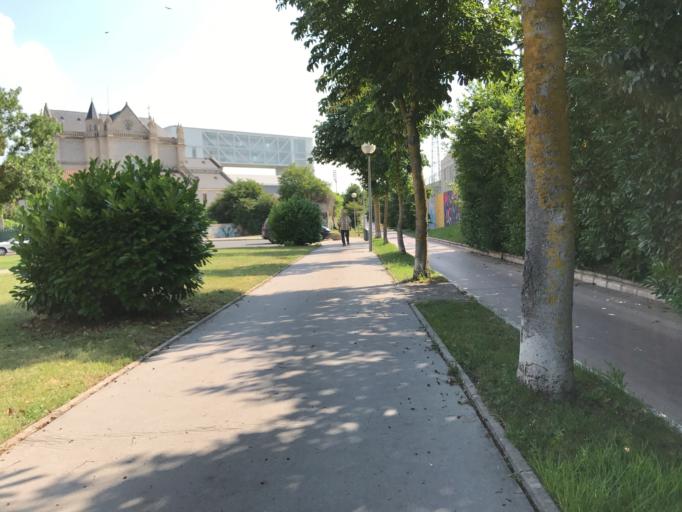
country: ES
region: Basque Country
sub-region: Provincia de Alava
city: Gasteiz / Vitoria
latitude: 42.8628
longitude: -2.6574
